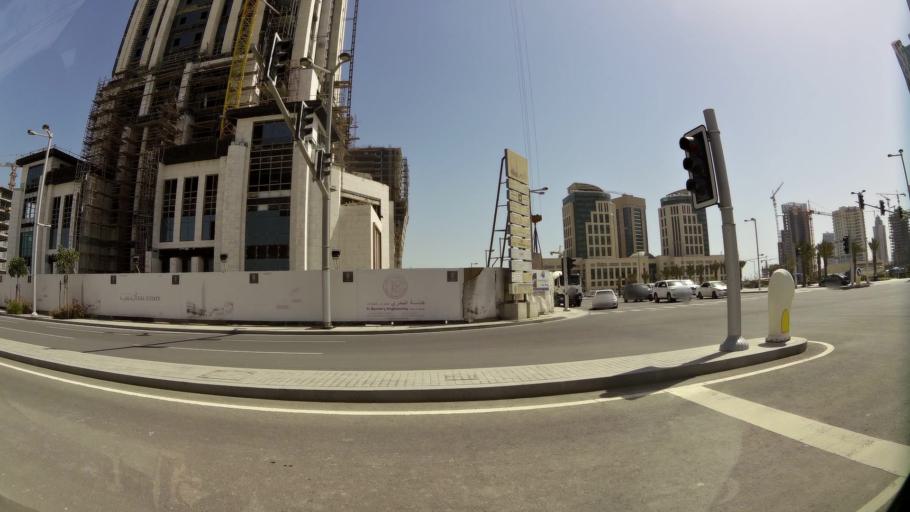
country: QA
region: Baladiyat ad Dawhah
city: Doha
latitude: 25.3938
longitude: 51.5185
